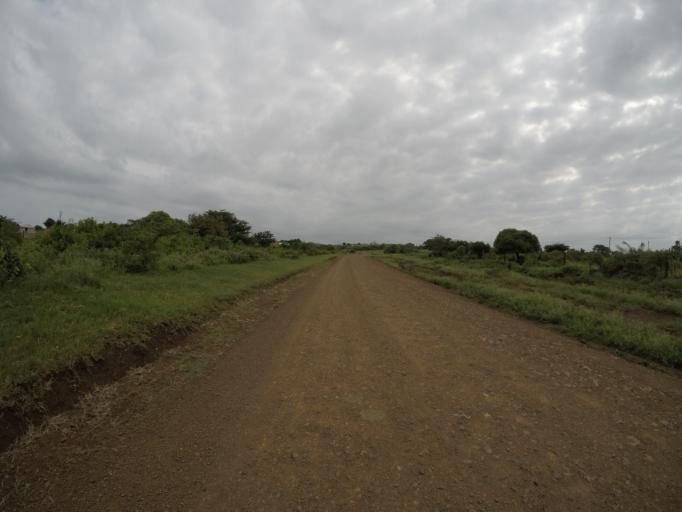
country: ZA
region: KwaZulu-Natal
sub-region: uThungulu District Municipality
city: Empangeni
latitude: -28.6419
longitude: 31.9047
